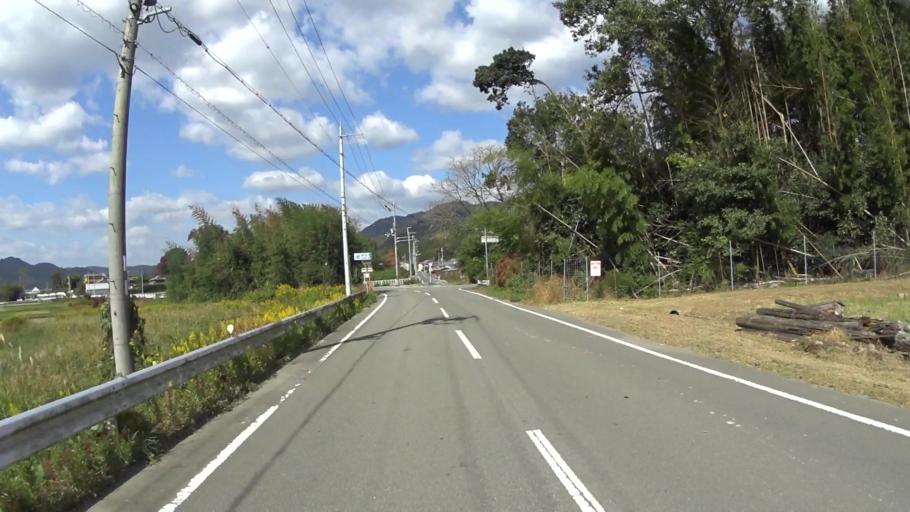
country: JP
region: Kyoto
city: Kameoka
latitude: 35.0884
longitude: 135.5593
